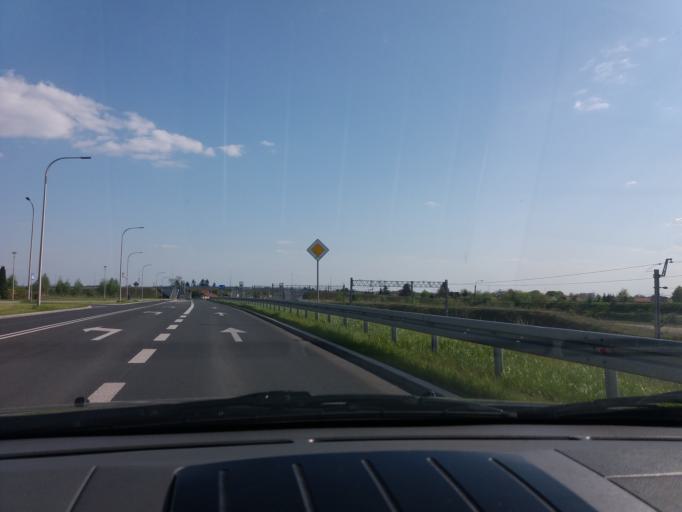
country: PL
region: Masovian Voivodeship
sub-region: Powiat mlawski
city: Mlawa
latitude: 53.1116
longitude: 20.3625
